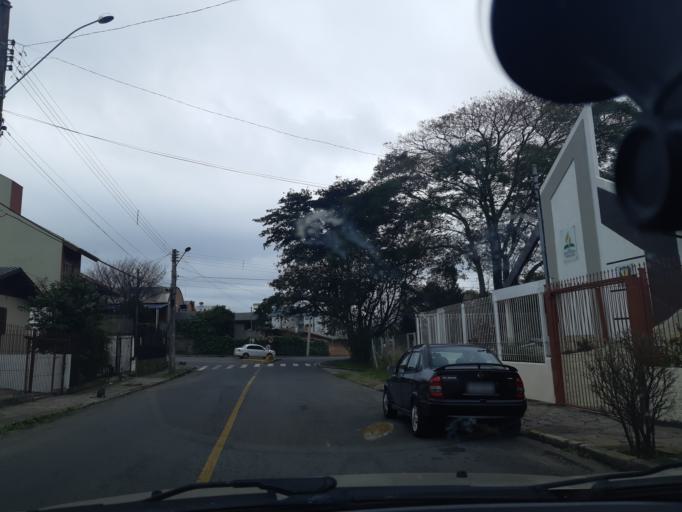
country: BR
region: Rio Grande do Sul
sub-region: Caxias Do Sul
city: Caxias do Sul
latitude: -29.1537
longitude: -51.2077
